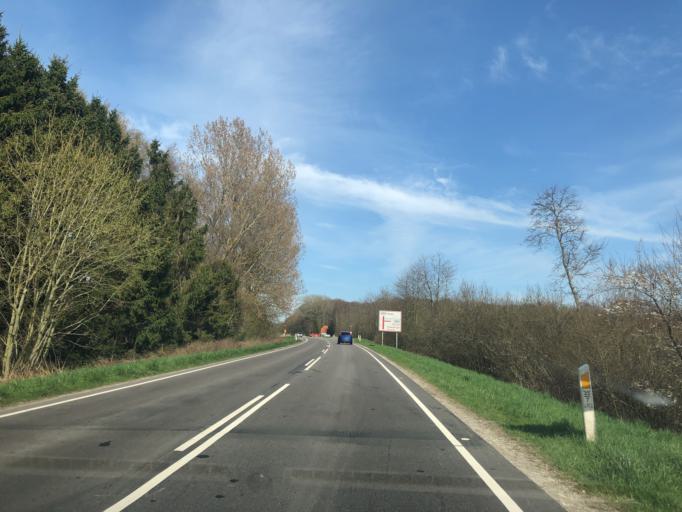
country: DK
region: Zealand
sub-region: Faxe Kommune
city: Fakse
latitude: 55.2792
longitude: 12.1674
